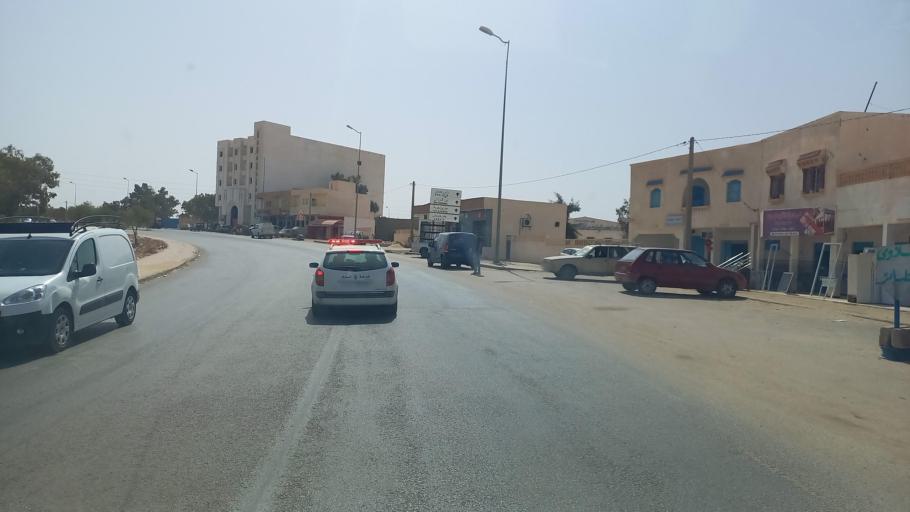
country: TN
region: Madanin
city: Medenine
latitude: 33.3422
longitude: 10.5042
